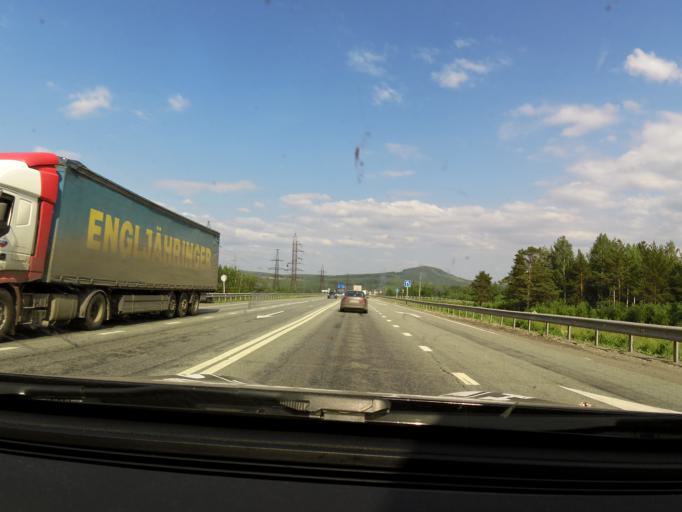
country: RU
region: Sverdlovsk
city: Revda
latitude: 56.8273
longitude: 59.9330
